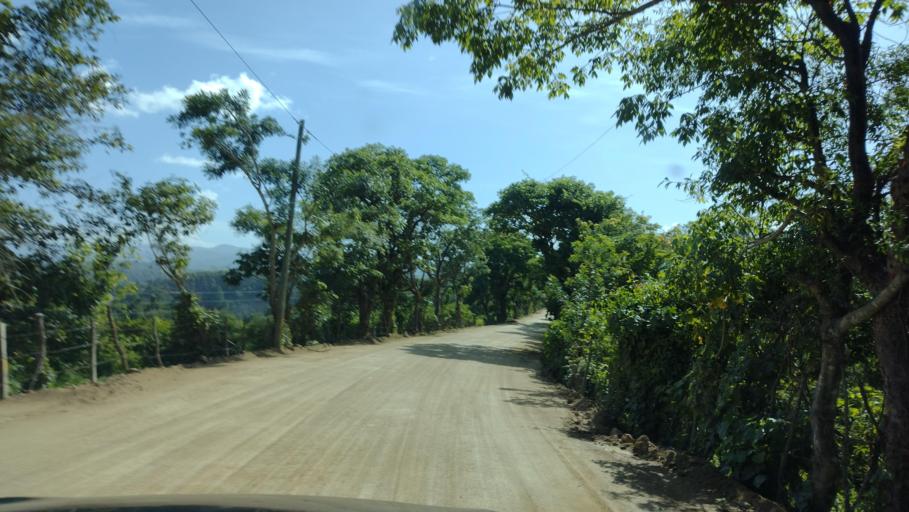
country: GT
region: Guatemala
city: Chinautla
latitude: 14.7560
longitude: -90.5171
